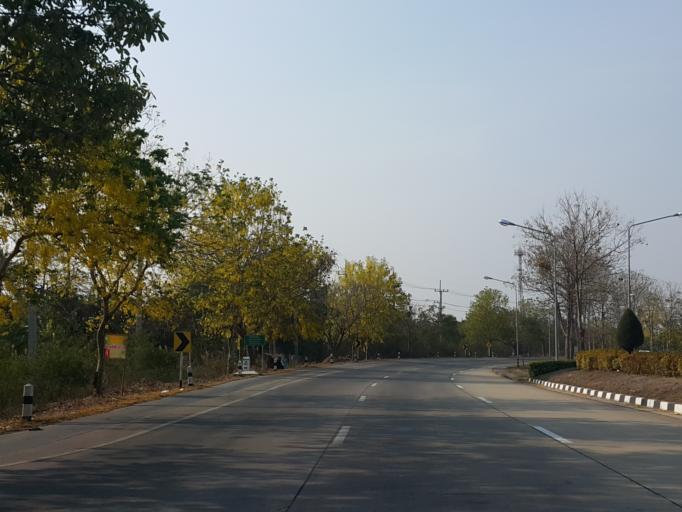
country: TH
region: Suphan Buri
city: Sam Chuk
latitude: 14.7835
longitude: 100.0882
